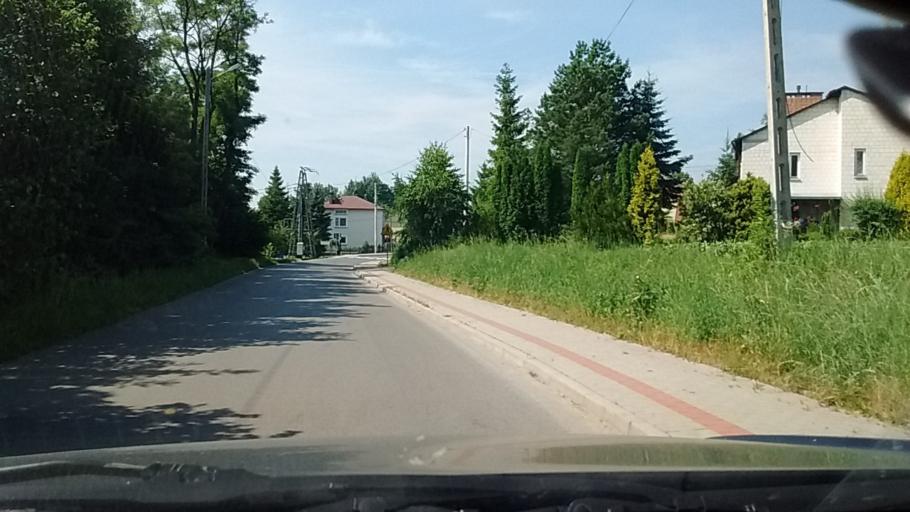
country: PL
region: Subcarpathian Voivodeship
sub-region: Powiat lancucki
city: Sonina
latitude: 50.0541
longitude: 22.2643
